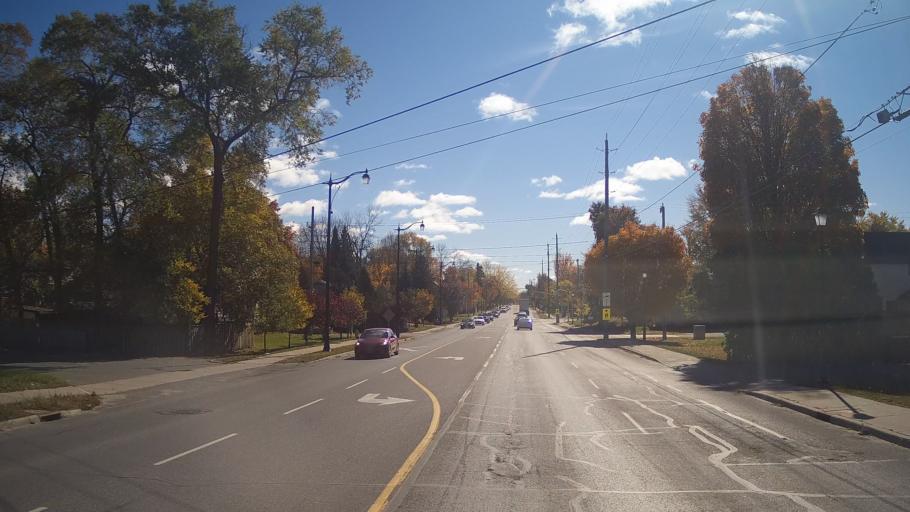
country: CA
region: Ontario
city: Perth
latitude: 44.9067
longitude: -76.2603
